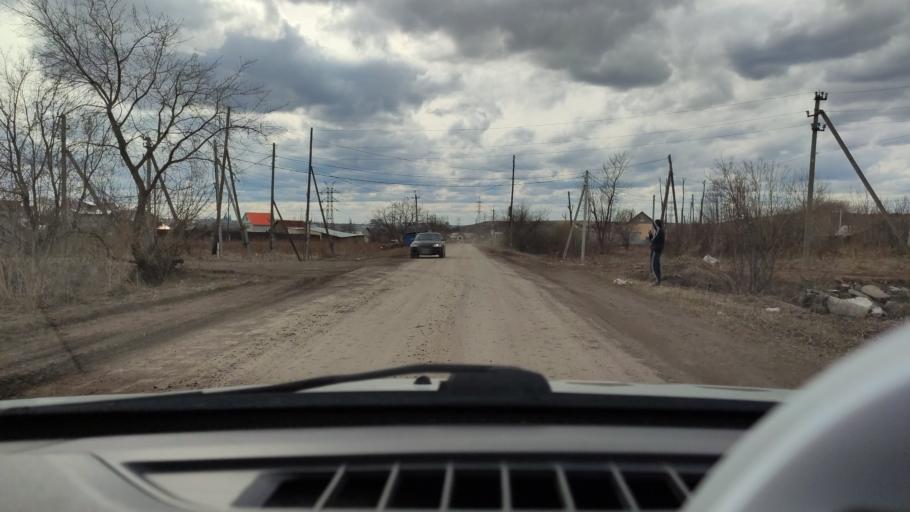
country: RU
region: Perm
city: Froly
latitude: 57.9301
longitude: 56.2429
